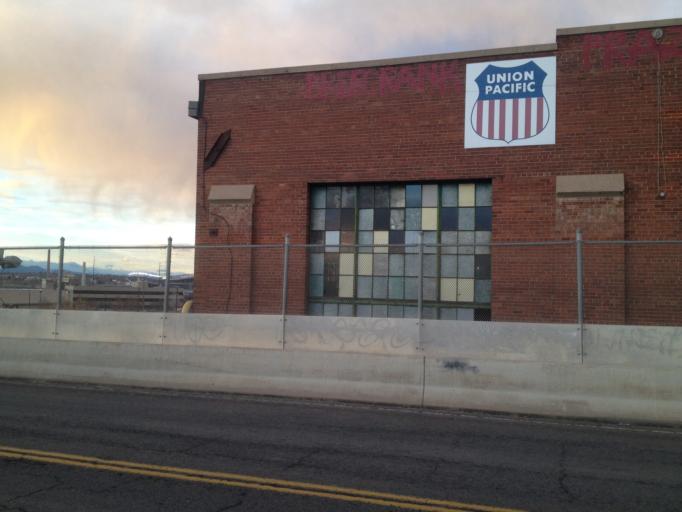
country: US
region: Colorado
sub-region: Denver County
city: Denver
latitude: 39.7283
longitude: -105.0065
